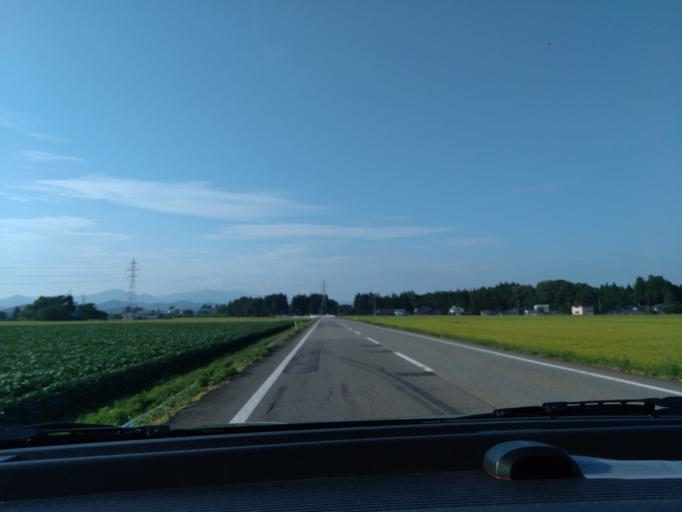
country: JP
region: Akita
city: Kakunodatemachi
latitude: 39.5355
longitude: 140.5582
